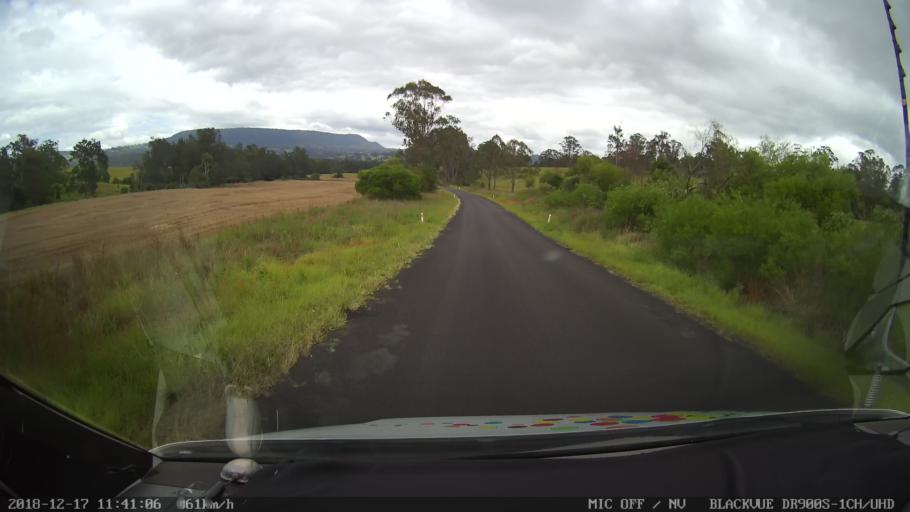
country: AU
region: New South Wales
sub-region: Kyogle
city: Kyogle
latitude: -28.6770
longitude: 152.5905
